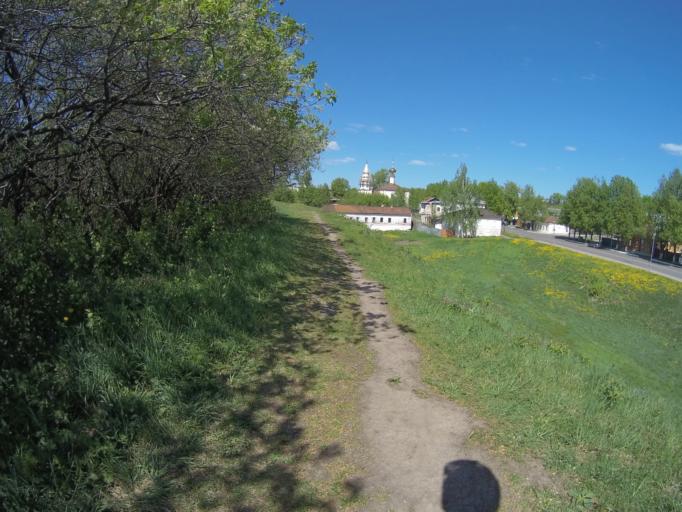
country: RU
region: Vladimir
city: Suzdal'
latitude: 56.4158
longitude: 40.4476
